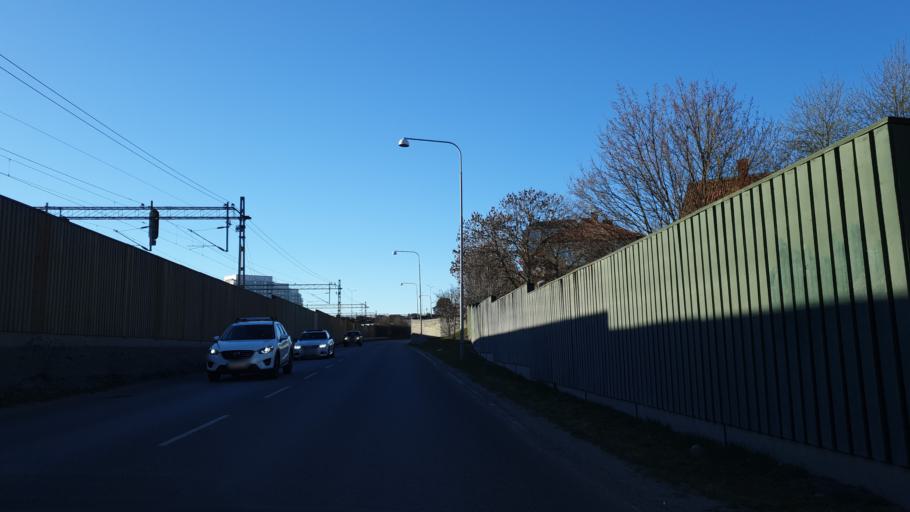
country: SE
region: Stockholm
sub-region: Solna Kommun
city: Solna
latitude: 59.3748
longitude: 18.0055
